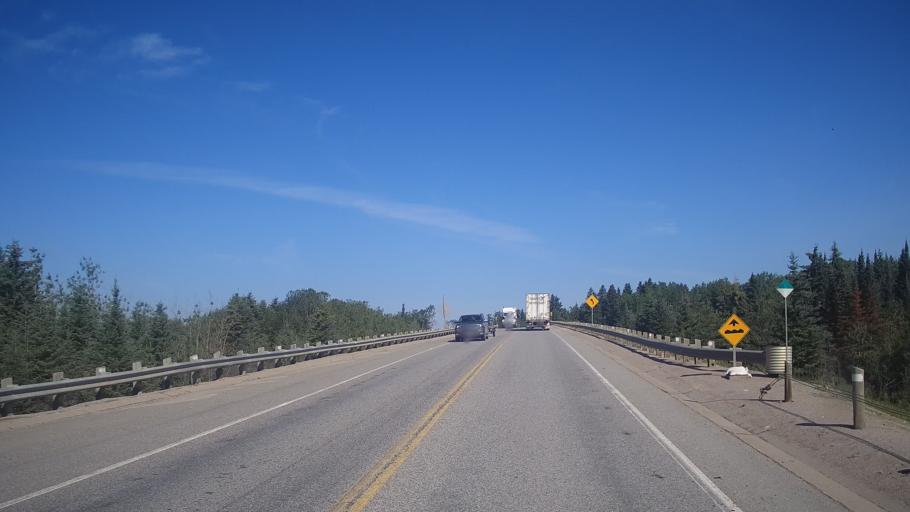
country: CA
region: Ontario
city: Dryden
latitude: 49.6891
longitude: -92.4961
